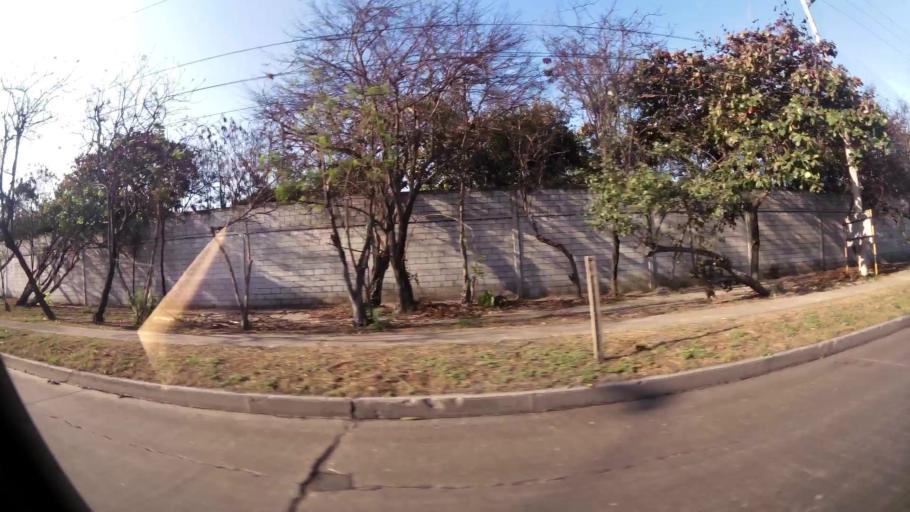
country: CO
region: Atlantico
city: Barranquilla
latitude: 11.0368
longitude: -74.8163
